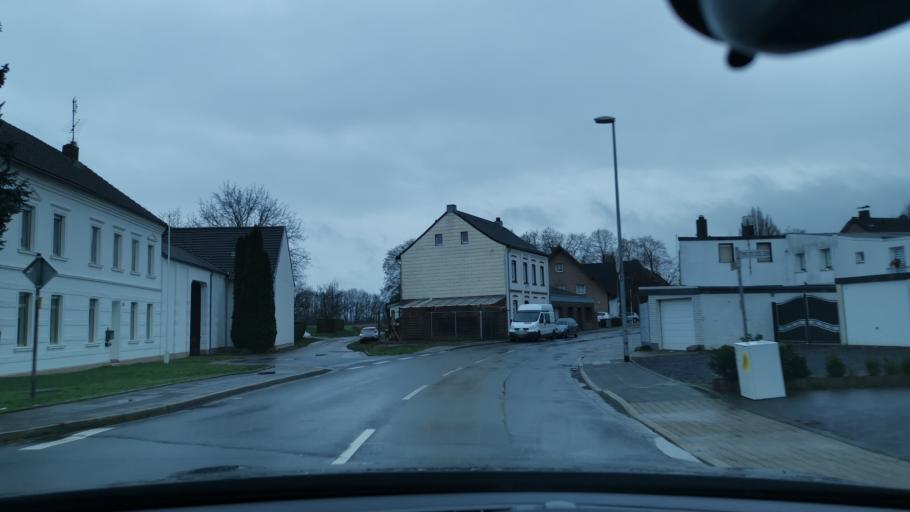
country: DE
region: North Rhine-Westphalia
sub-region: Regierungsbezirk Koln
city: Titz
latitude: 51.0036
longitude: 6.4874
